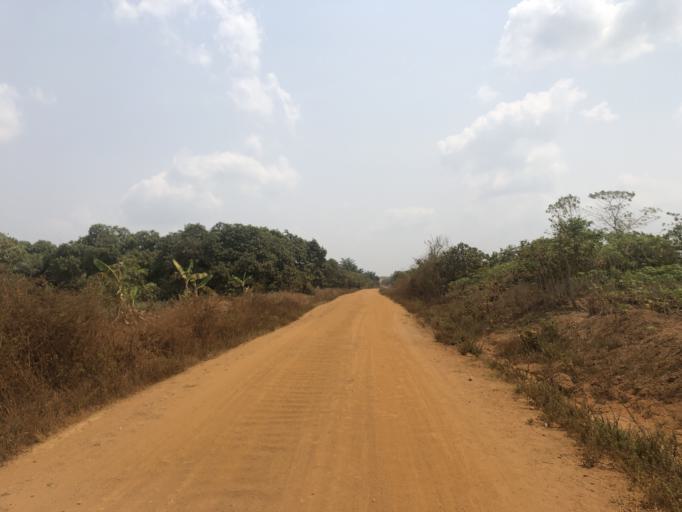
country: NG
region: Osun
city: Bode Osi
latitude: 7.8027
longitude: 4.1605
